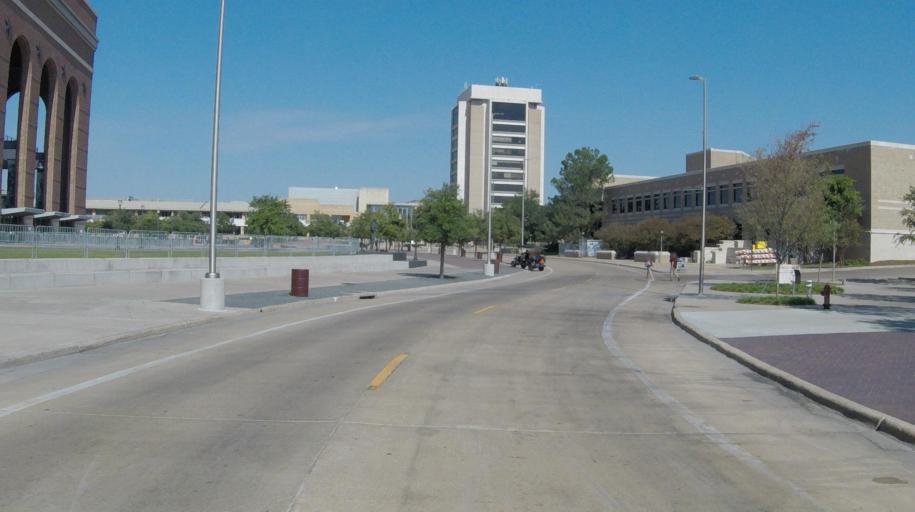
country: US
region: Texas
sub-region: Brazos County
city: College Station
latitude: 30.6107
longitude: -96.3392
